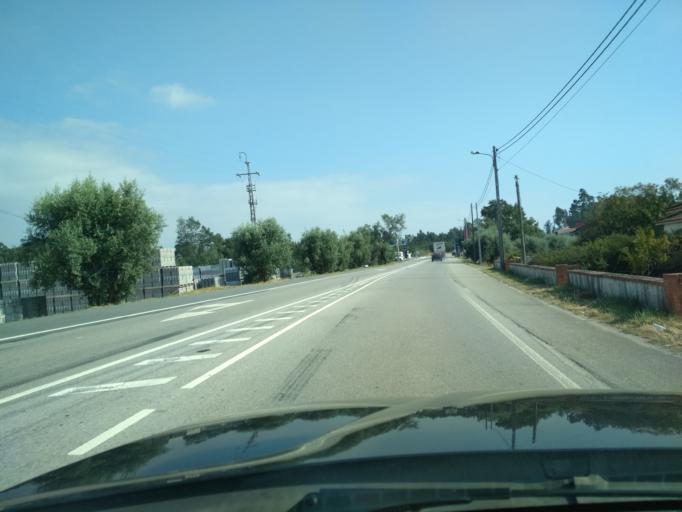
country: PT
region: Aveiro
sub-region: Mealhada
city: Pampilhosa do Botao
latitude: 40.3354
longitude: -8.4508
